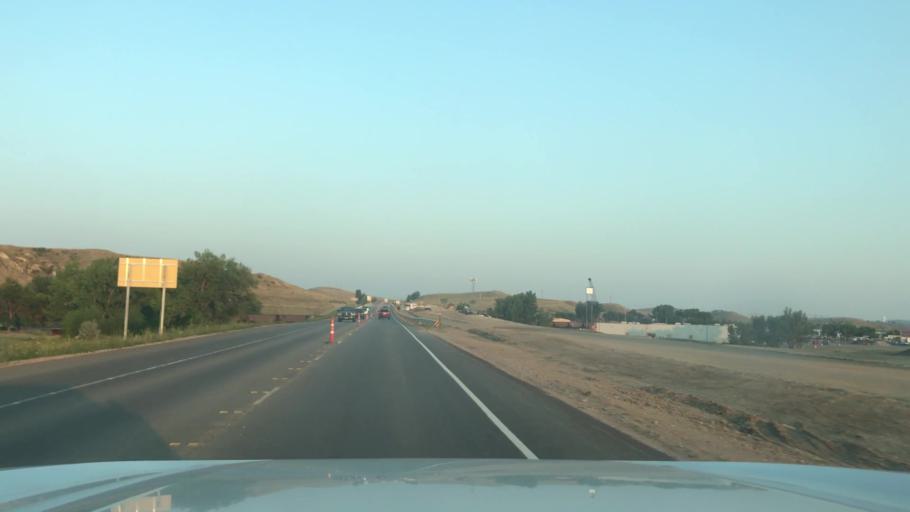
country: US
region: Wyoming
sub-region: Sheridan County
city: Sheridan
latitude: 44.8317
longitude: -106.9597
